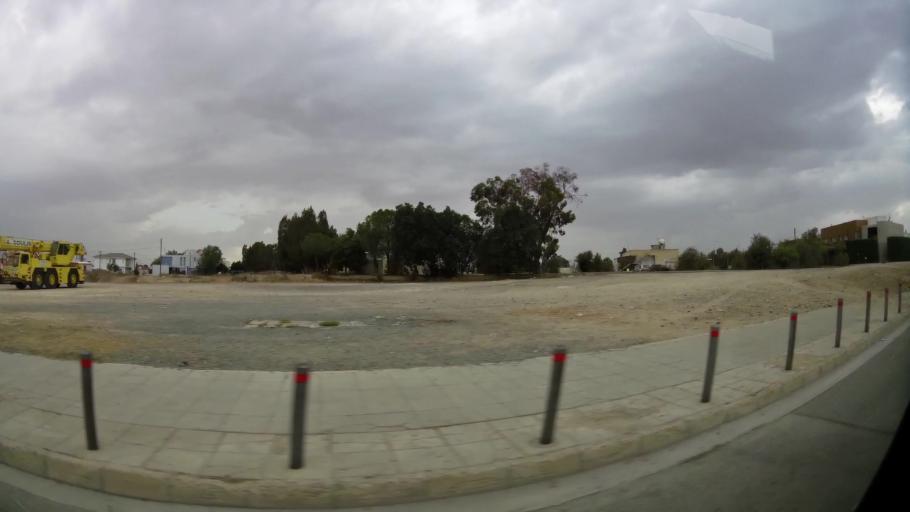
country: CY
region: Lefkosia
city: Nicosia
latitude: 35.1287
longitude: 33.3565
